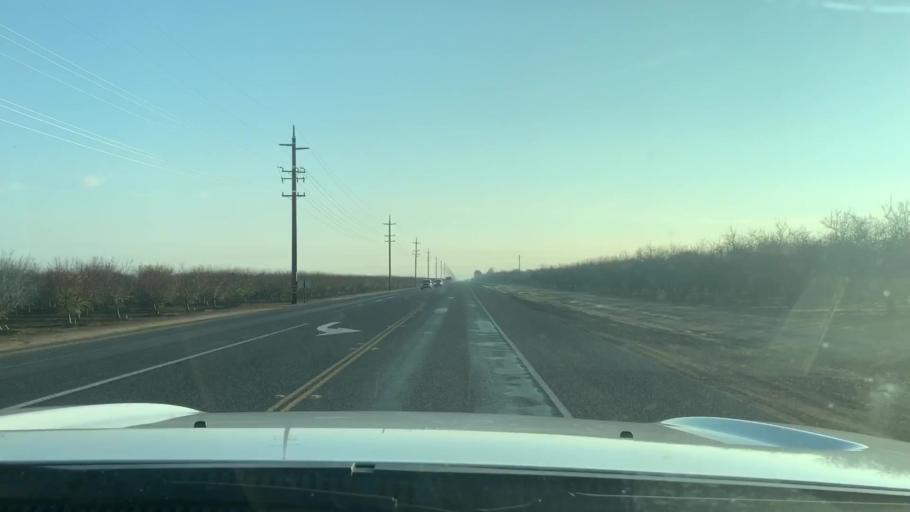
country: US
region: California
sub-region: Kern County
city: Wasco
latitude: 35.6014
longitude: -119.4366
